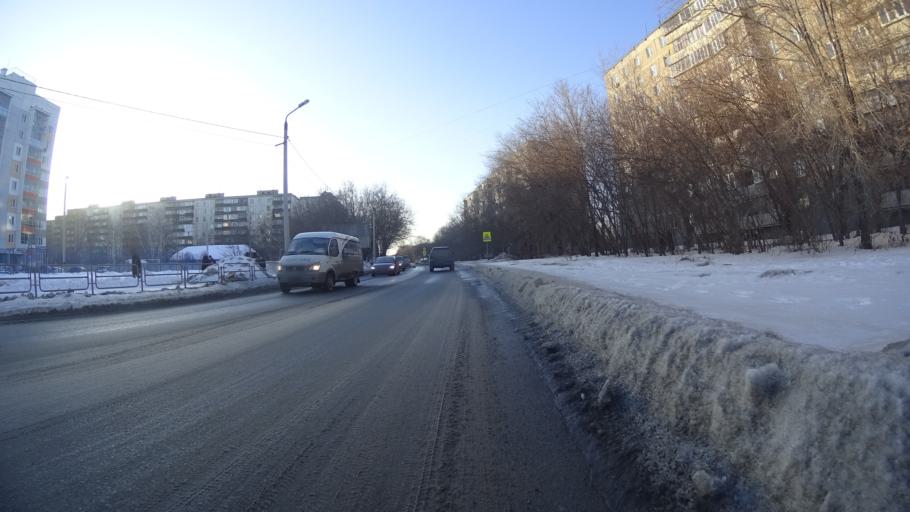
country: RU
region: Chelyabinsk
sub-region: Gorod Chelyabinsk
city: Chelyabinsk
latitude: 55.1378
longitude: 61.4474
